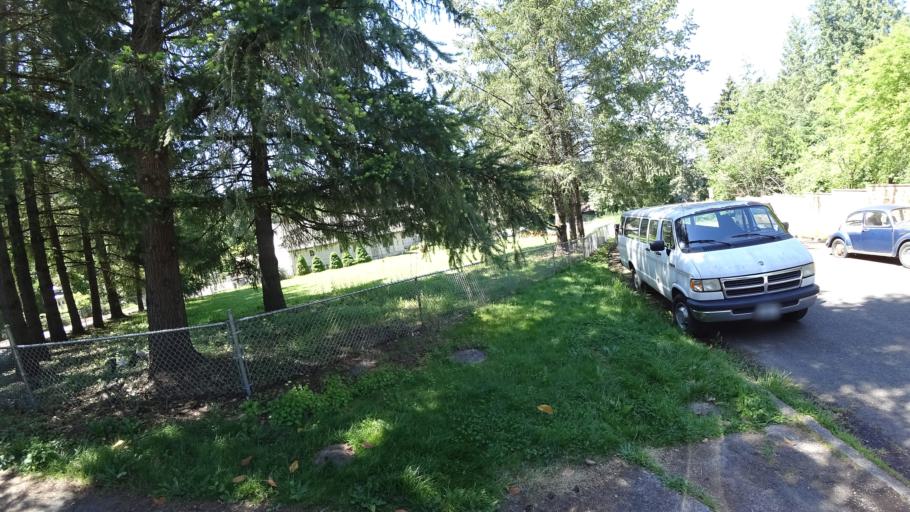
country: US
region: Oregon
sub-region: Washington County
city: Raleigh Hills
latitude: 45.4876
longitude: -122.7213
